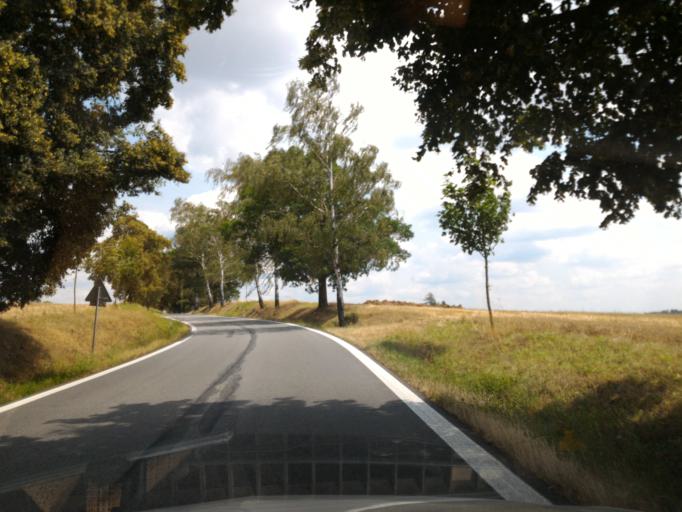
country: CZ
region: Vysocina
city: Pribyslav
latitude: 49.6013
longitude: 15.6703
